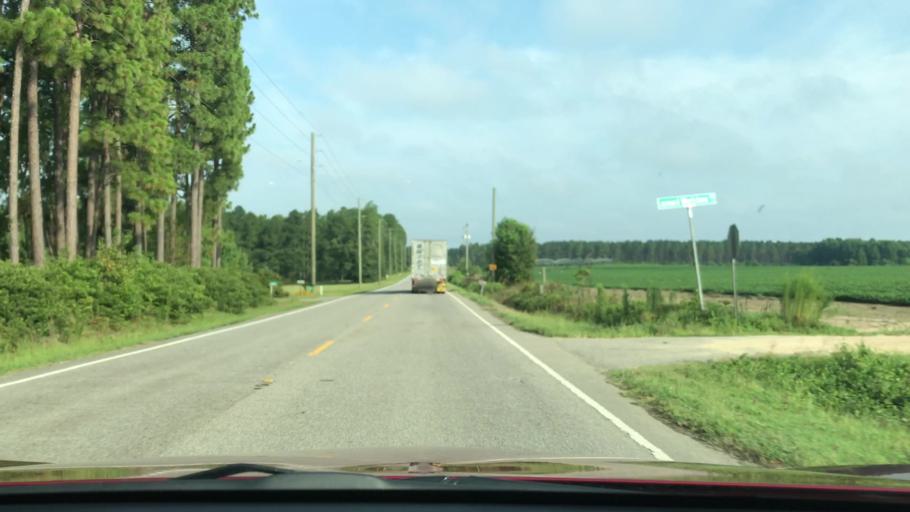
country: US
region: South Carolina
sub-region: Barnwell County
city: Williston
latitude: 33.6110
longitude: -81.2768
